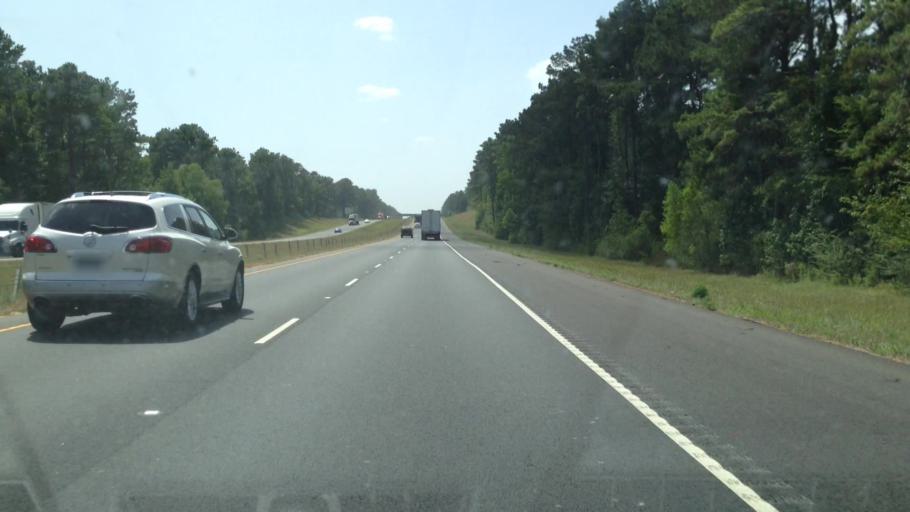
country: US
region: Louisiana
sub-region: Webster Parish
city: Minden
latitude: 32.5746
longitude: -93.2193
